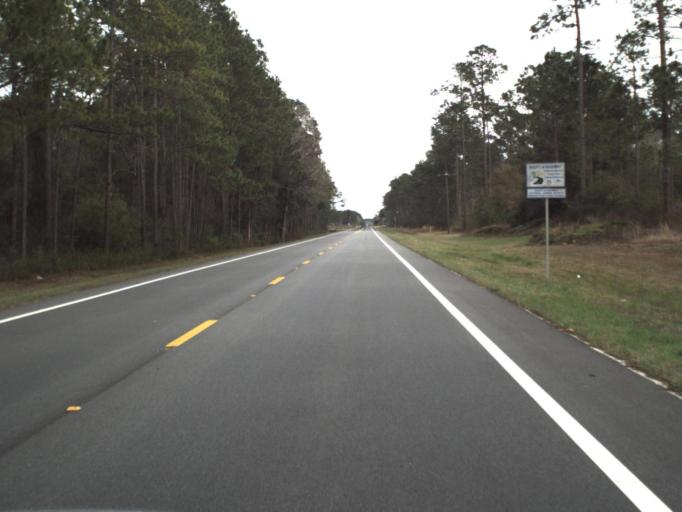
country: US
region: Florida
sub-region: Gulf County
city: Wewahitchka
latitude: 30.1342
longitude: -85.2382
